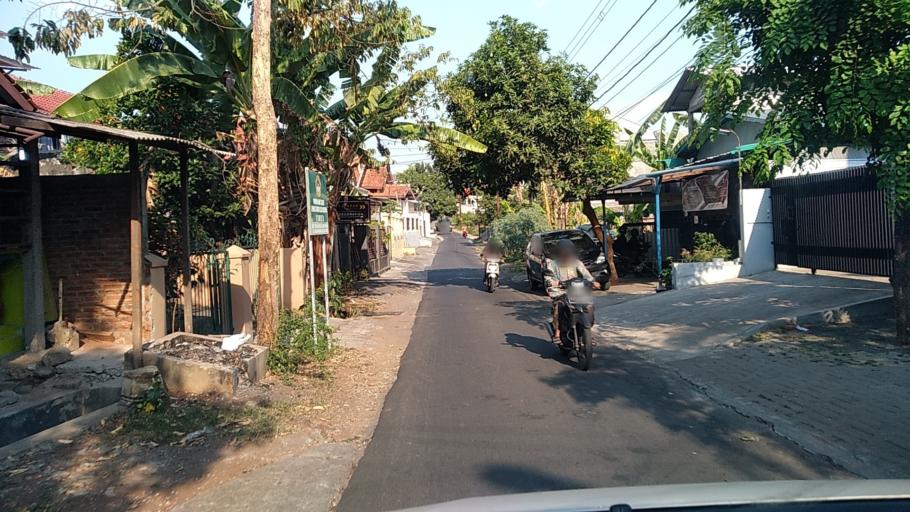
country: ID
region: Central Java
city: Ungaran
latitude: -7.0705
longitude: 110.4332
